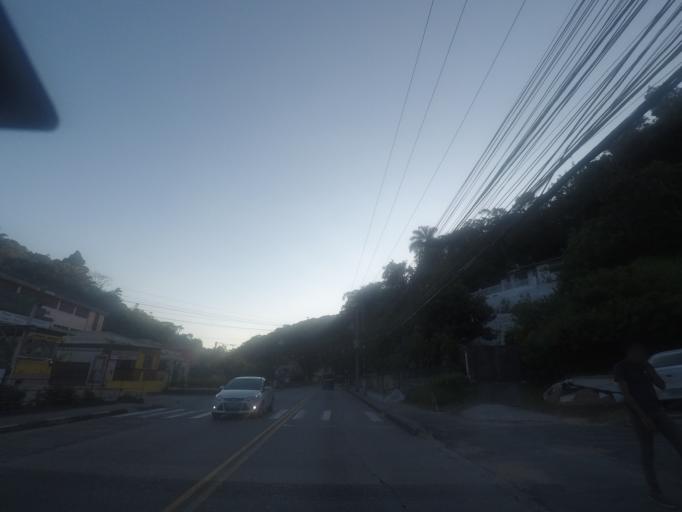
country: BR
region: Rio de Janeiro
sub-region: Petropolis
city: Petropolis
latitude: -22.5335
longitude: -43.2058
